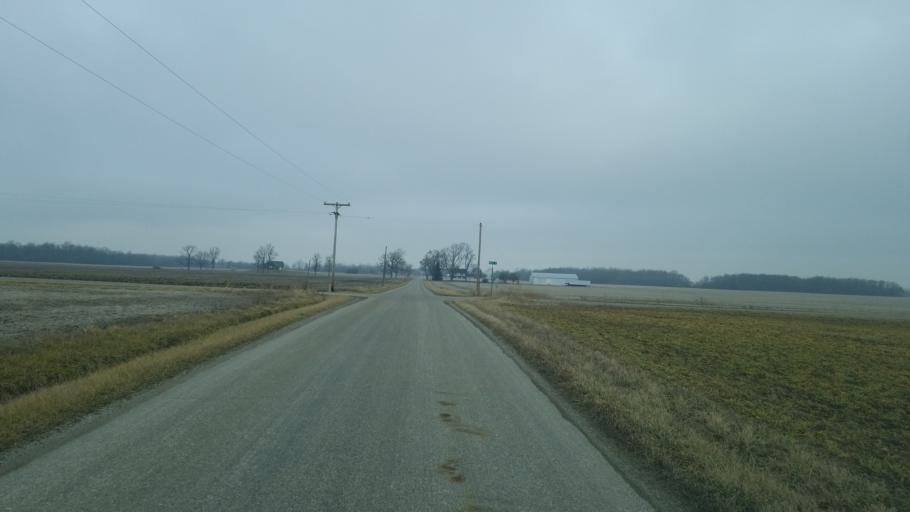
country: US
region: Indiana
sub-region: Adams County
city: Berne
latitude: 40.6879
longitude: -84.8550
